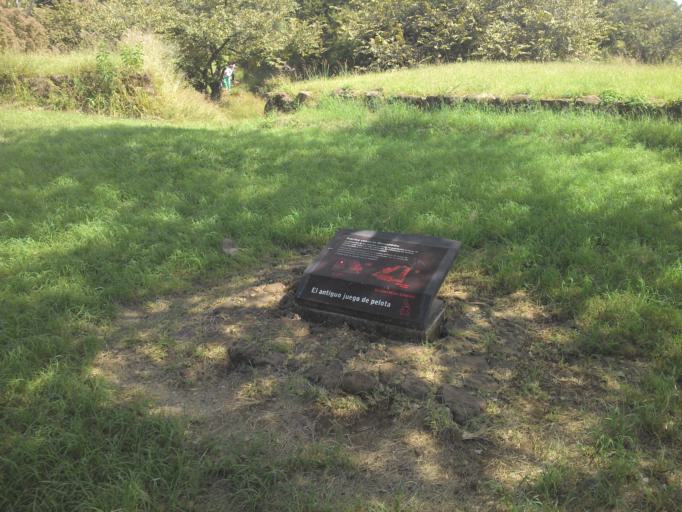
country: MX
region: Jalisco
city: Teuchitlan
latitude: 20.6957
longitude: -103.8362
